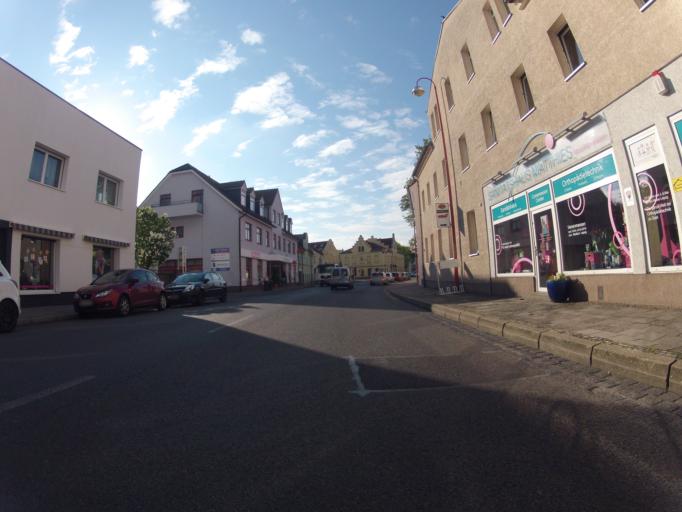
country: DE
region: Saxony
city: Grossposna
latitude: 51.2828
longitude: 12.4602
